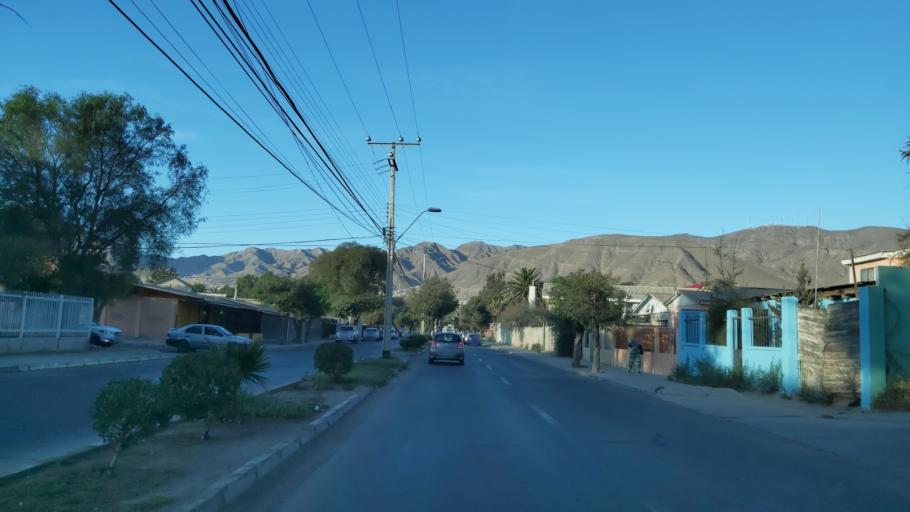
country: CL
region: Atacama
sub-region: Provincia de Copiapo
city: Copiapo
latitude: -27.3771
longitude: -70.3176
